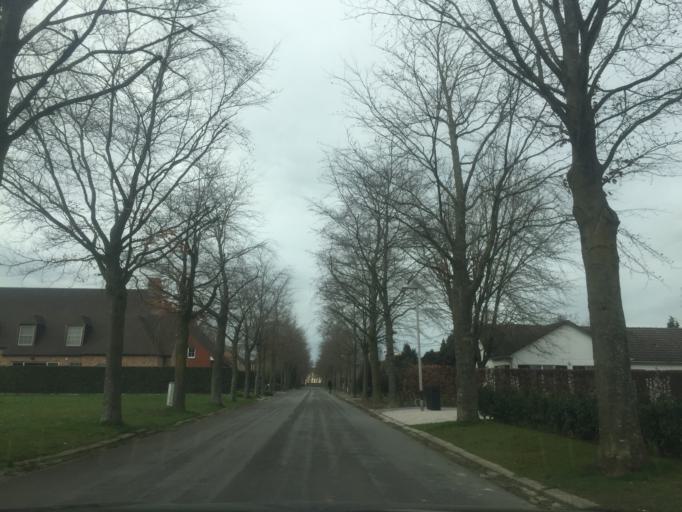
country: BE
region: Flanders
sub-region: Provincie West-Vlaanderen
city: Wielsbeke
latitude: 50.9119
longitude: 3.3769
